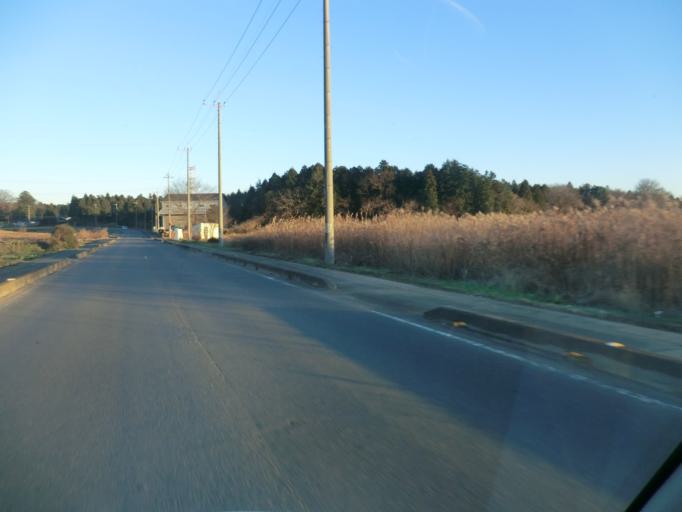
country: JP
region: Ibaraki
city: Mitsukaido
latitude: 36.0693
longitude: 140.0272
